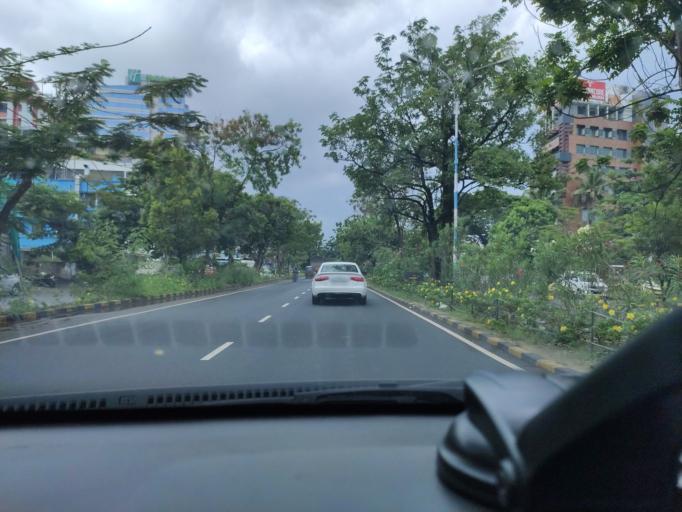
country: IN
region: Kerala
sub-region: Ernakulam
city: Cochin
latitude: 9.9919
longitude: 76.3152
